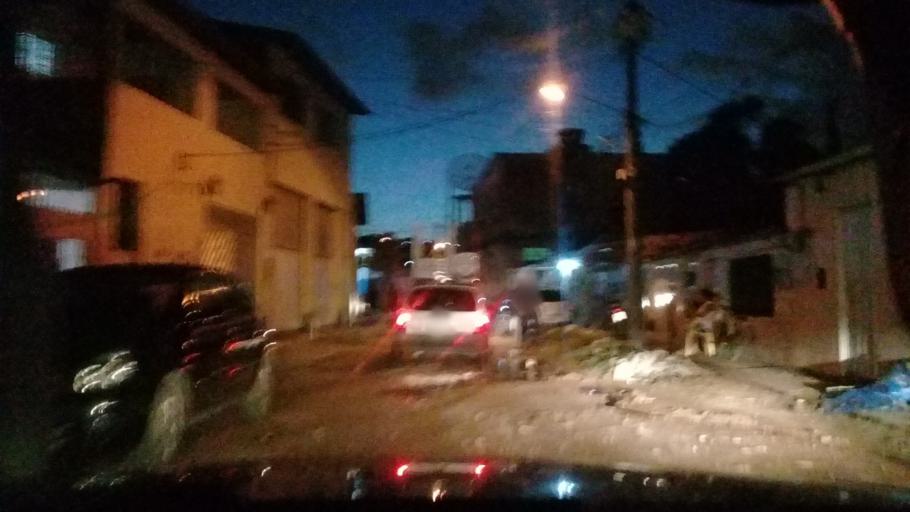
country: BR
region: Pernambuco
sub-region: Jaboatao Dos Guararapes
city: Jaboatao dos Guararapes
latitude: -8.1144
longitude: -34.9402
